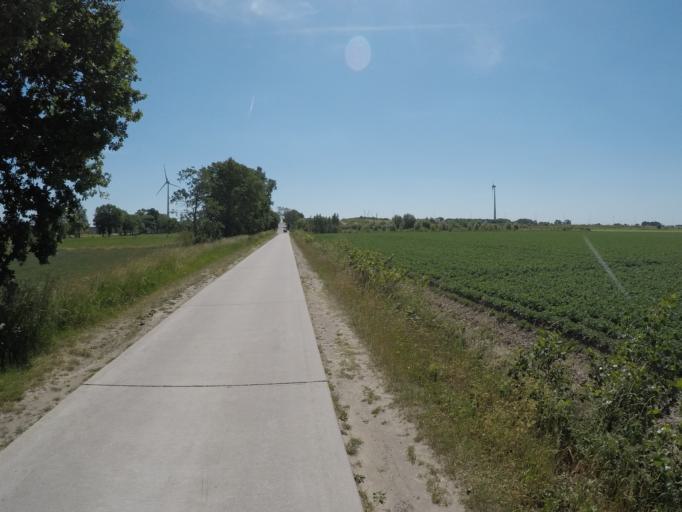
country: BE
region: Flanders
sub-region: Provincie Antwerpen
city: Hoogstraten
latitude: 51.4161
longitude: 4.6962
